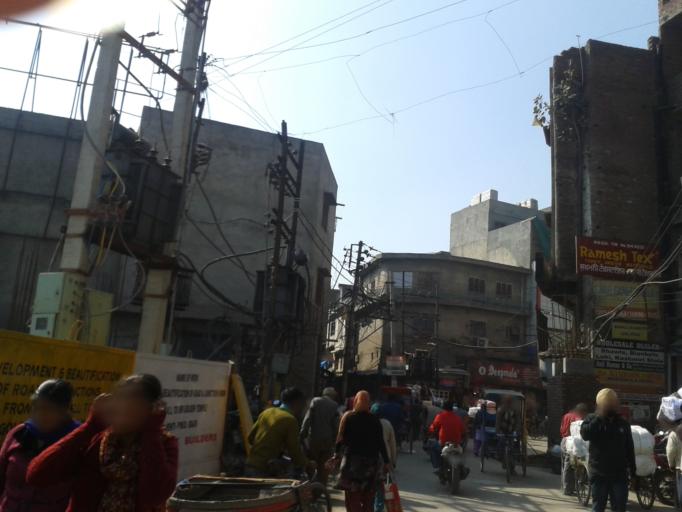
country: IN
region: Punjab
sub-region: Amritsar
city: Amritsar
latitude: 31.6257
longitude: 74.8776
